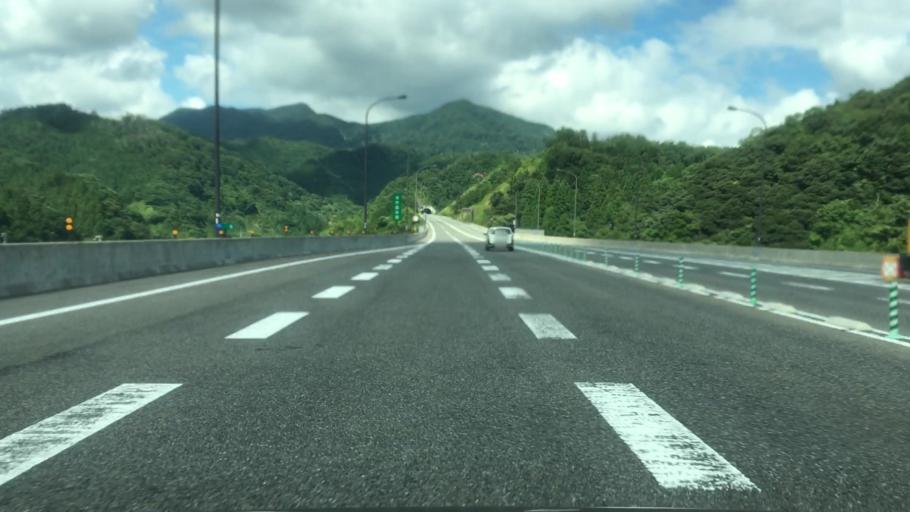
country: JP
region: Hyogo
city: Toyooka
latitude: 35.6296
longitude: 134.6221
